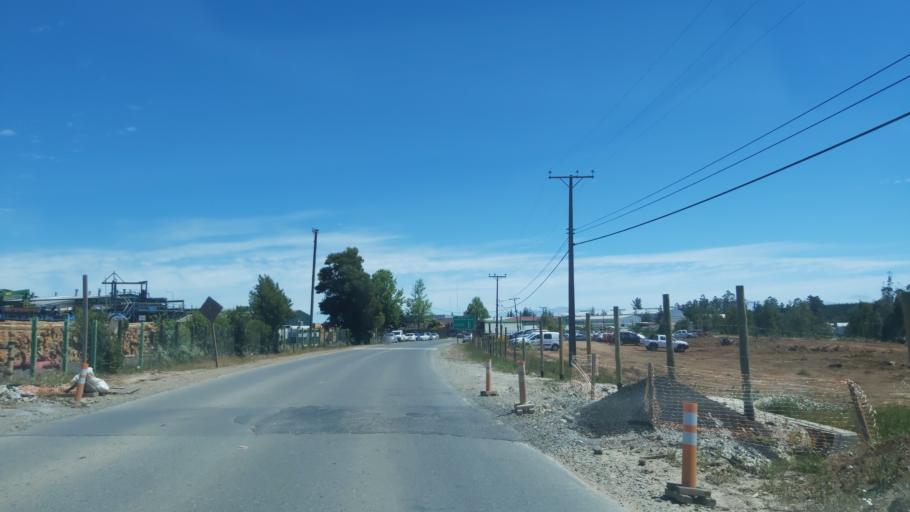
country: CL
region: Maule
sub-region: Provincia de Talca
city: Constitucion
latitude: -35.3724
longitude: -72.4139
